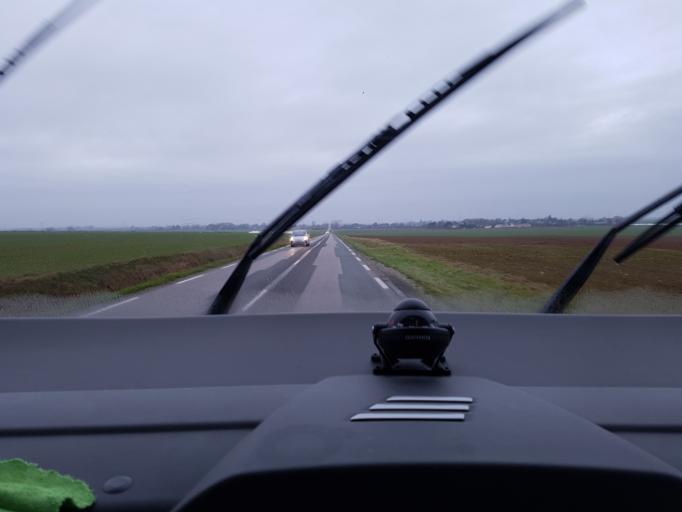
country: FR
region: Haute-Normandie
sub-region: Departement de l'Eure
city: Beaumont-le-Roger
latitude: 49.1022
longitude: 0.8232
